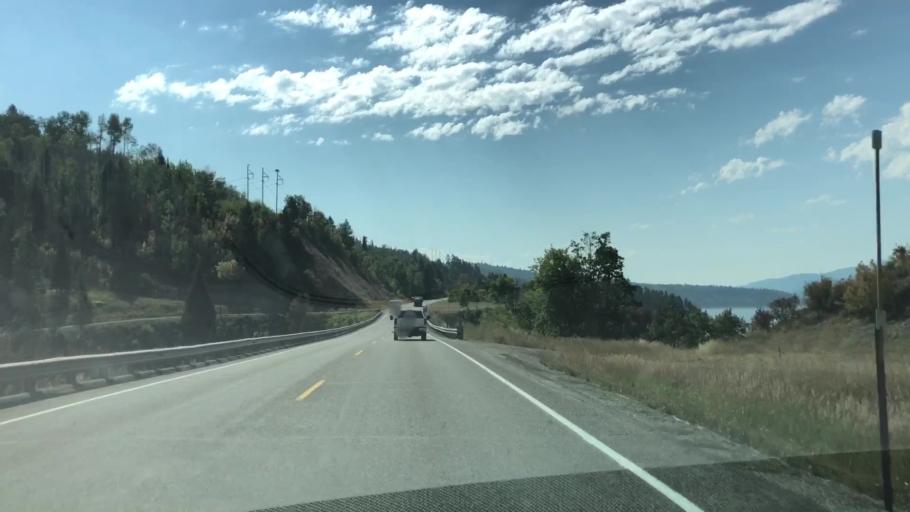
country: US
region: Idaho
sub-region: Teton County
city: Victor
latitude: 43.2948
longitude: -111.1266
